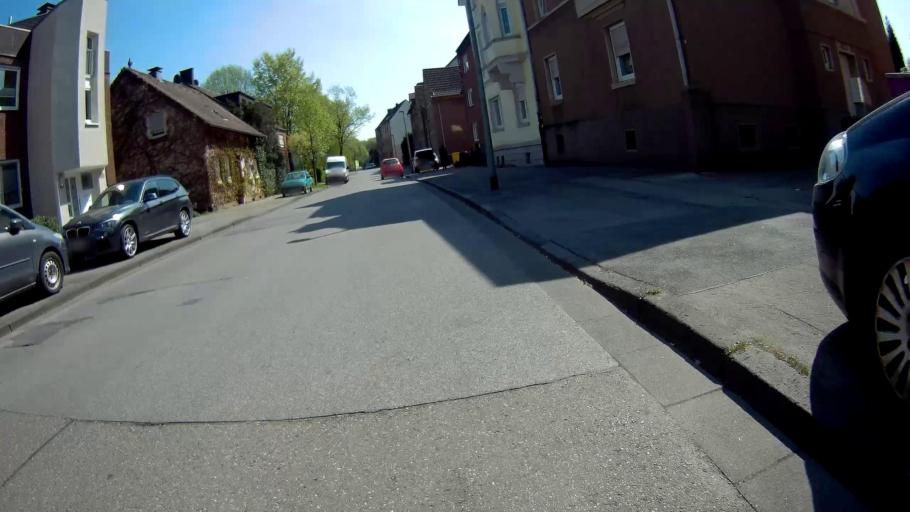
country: DE
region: North Rhine-Westphalia
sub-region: Regierungsbezirk Munster
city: Gladbeck
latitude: 51.5484
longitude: 7.0452
